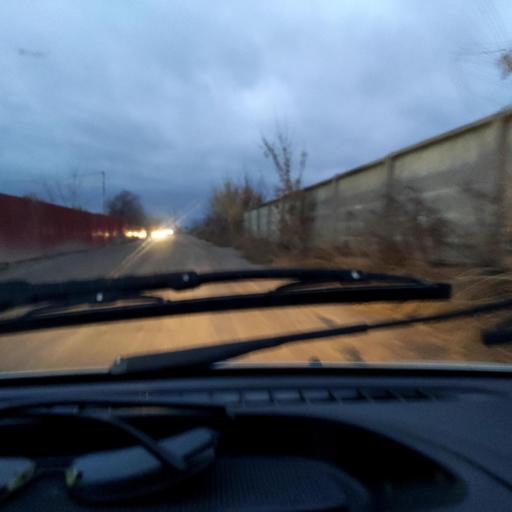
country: RU
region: Samara
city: Tol'yatti
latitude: 53.5664
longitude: 49.4835
